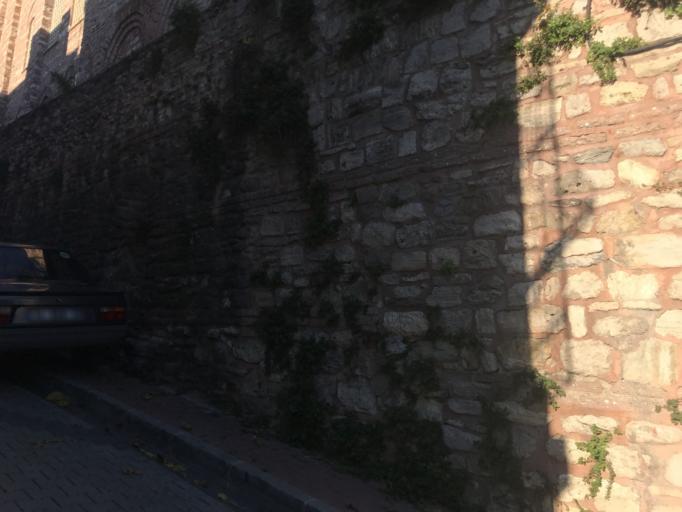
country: TR
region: Istanbul
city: Istanbul
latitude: 41.0265
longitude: 28.9563
